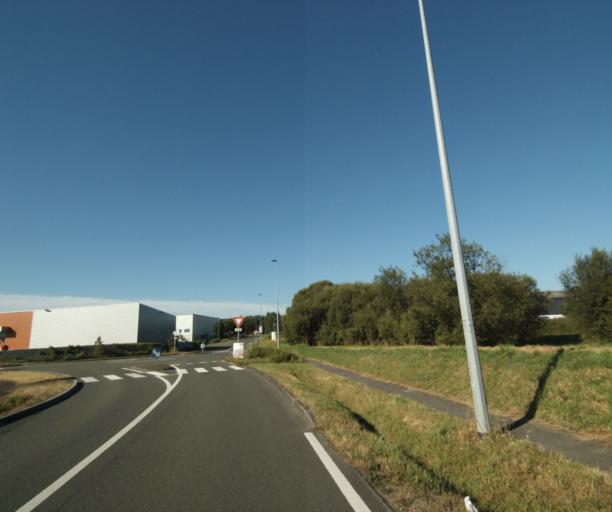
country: FR
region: Pays de la Loire
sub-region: Departement de la Mayenne
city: Laval
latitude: 48.0555
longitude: -0.7387
